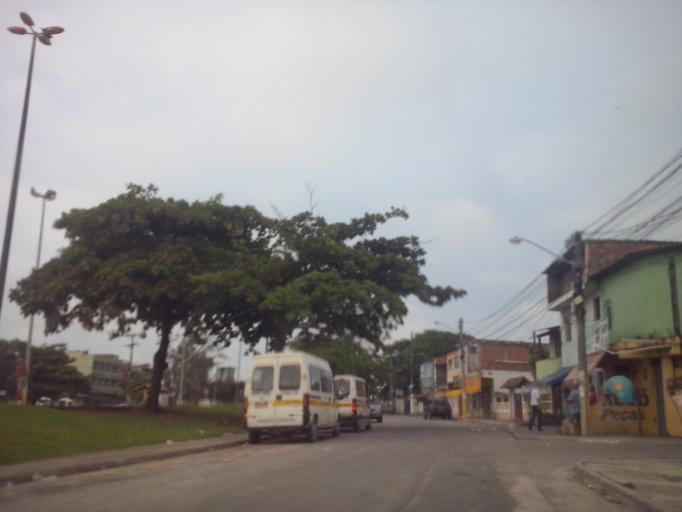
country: BR
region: Rio de Janeiro
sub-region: Rio Das Ostras
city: Rio das Ostras
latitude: -22.5605
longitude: -41.9813
